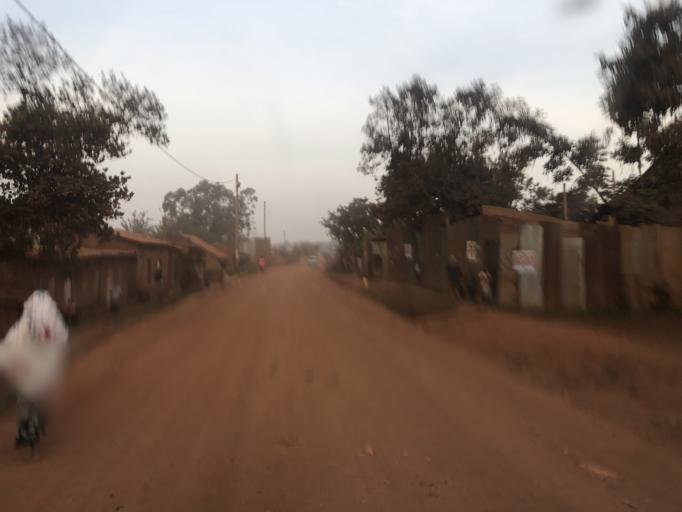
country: UG
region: Central Region
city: Kampala Central Division
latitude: 0.2997
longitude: 32.5166
